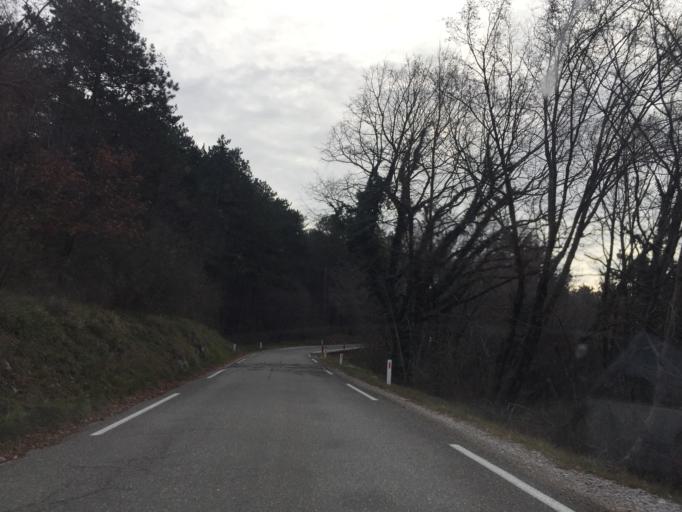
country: SI
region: Nova Gorica
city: Kromberk
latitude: 45.9788
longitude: 13.7156
